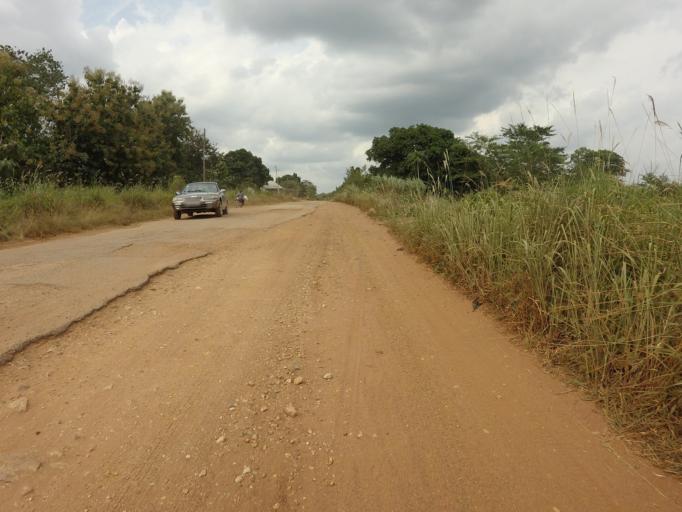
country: GH
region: Volta
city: Ho
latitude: 6.6542
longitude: 0.3438
